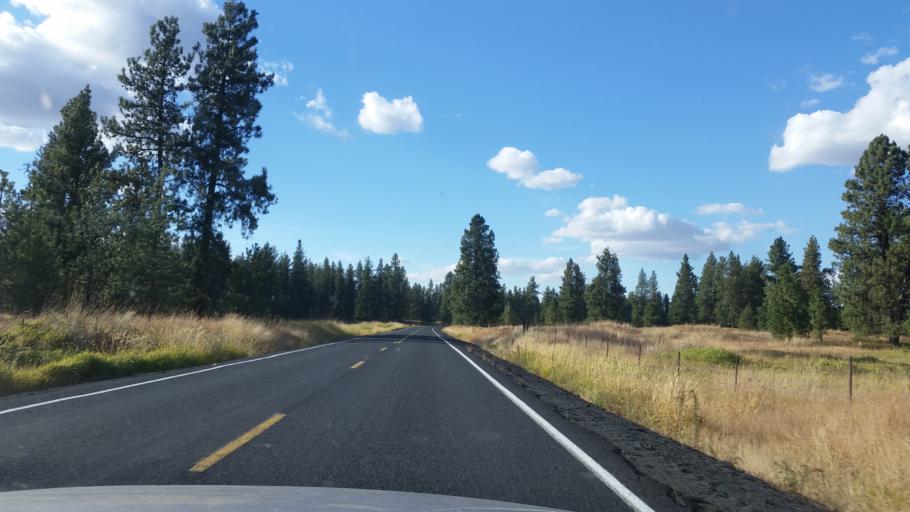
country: US
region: Washington
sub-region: Spokane County
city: Cheney
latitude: 47.4386
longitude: -117.5727
